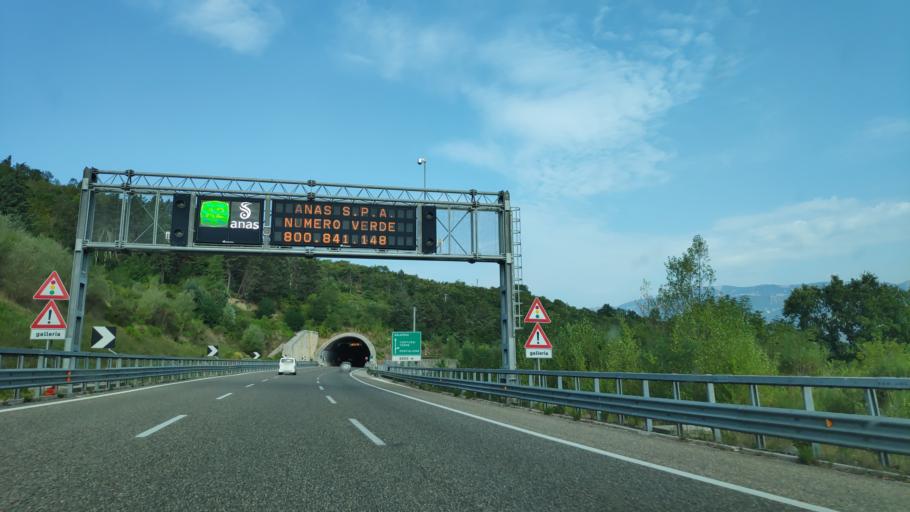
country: IT
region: Campania
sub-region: Provincia di Salerno
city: Contursi Terme
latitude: 40.6129
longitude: 15.2528
